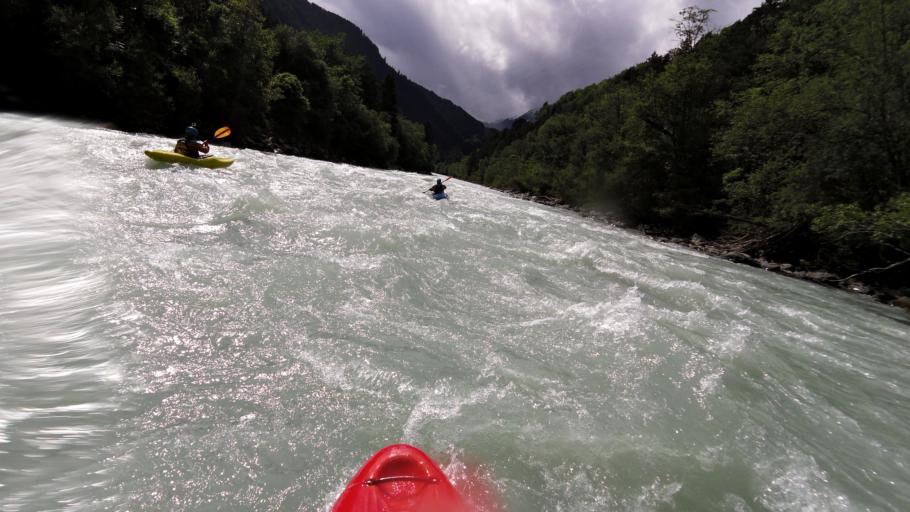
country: AT
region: Tyrol
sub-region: Politischer Bezirk Landeck
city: Landeck
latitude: 47.1231
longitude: 10.5965
